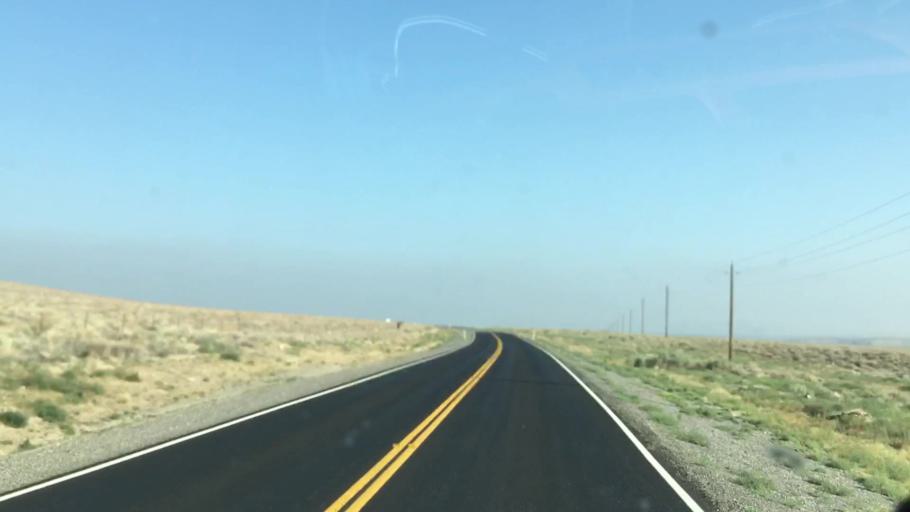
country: US
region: Nevada
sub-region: Lyon County
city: Fernley
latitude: 39.7703
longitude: -119.3441
